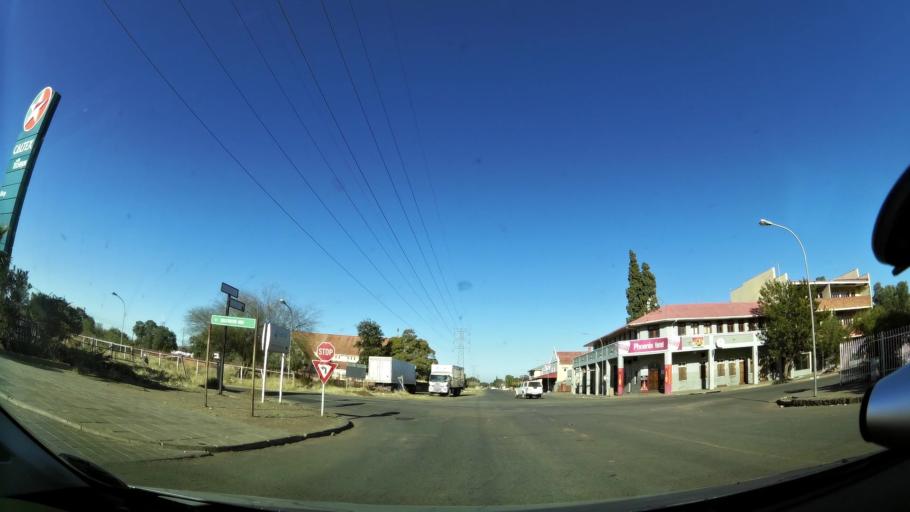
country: ZA
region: Northern Cape
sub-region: Frances Baard District Municipality
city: Kimberley
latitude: -28.7584
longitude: 24.7856
